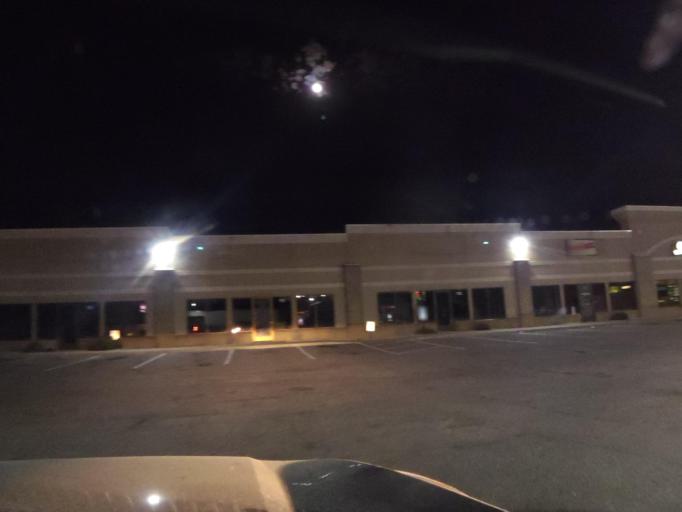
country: US
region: Minnesota
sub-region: Stearns County
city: Saint Augusta
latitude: 45.4959
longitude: -94.1483
